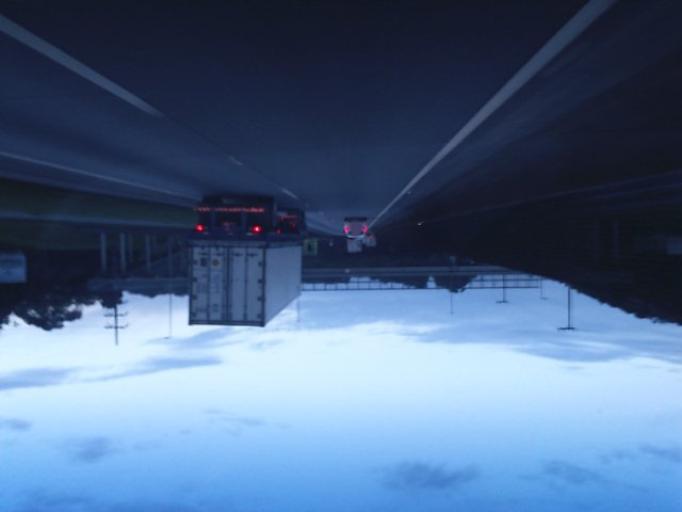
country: BR
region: Santa Catarina
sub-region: Joinville
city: Joinville
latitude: -26.3086
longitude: -48.8789
